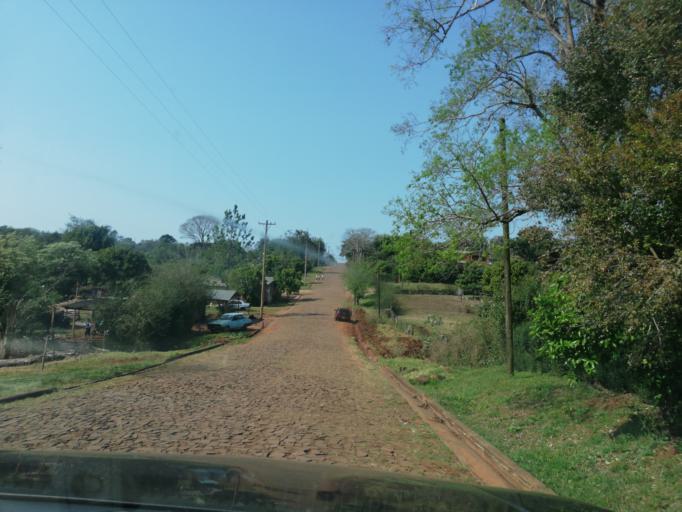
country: AR
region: Misiones
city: Bonpland
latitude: -27.4809
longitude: -55.4798
